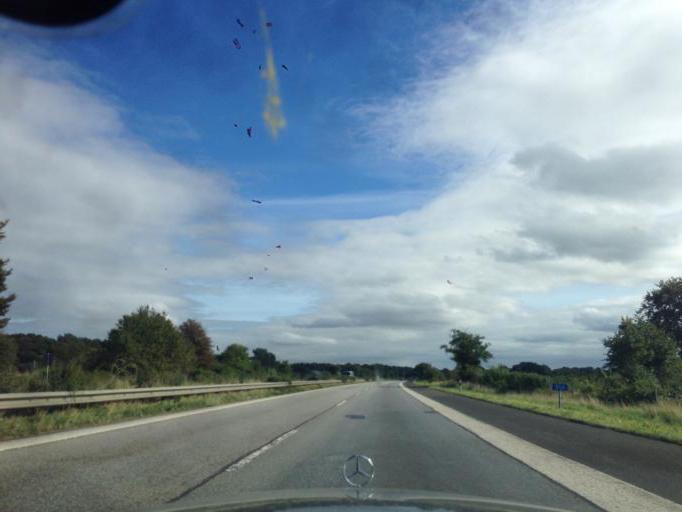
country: DE
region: Schleswig-Holstein
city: Brekendorf
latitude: 54.3960
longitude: 9.6461
